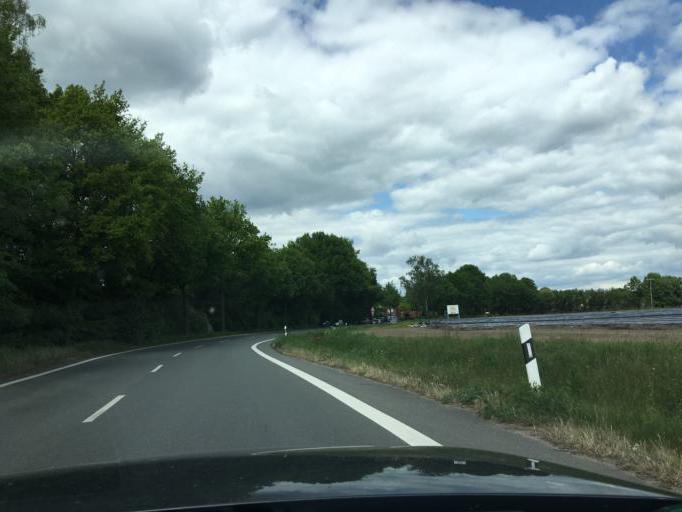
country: DE
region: North Rhine-Westphalia
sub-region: Regierungsbezirk Munster
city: Muenster
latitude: 52.0269
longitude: 7.6792
